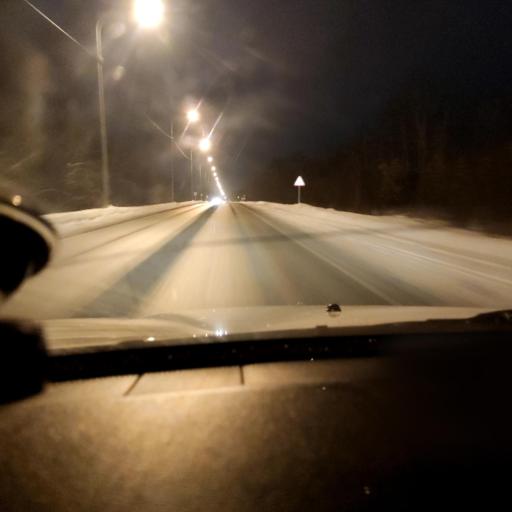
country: RU
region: Samara
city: Petra-Dubrava
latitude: 53.2773
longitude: 50.3806
